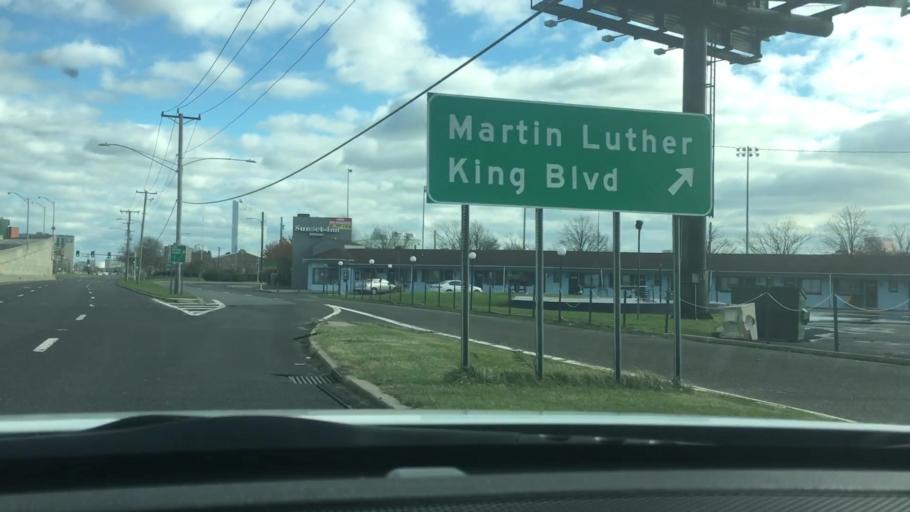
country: US
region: New Jersey
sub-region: Atlantic County
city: Atlantic City
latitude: 39.3741
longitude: -74.4420
